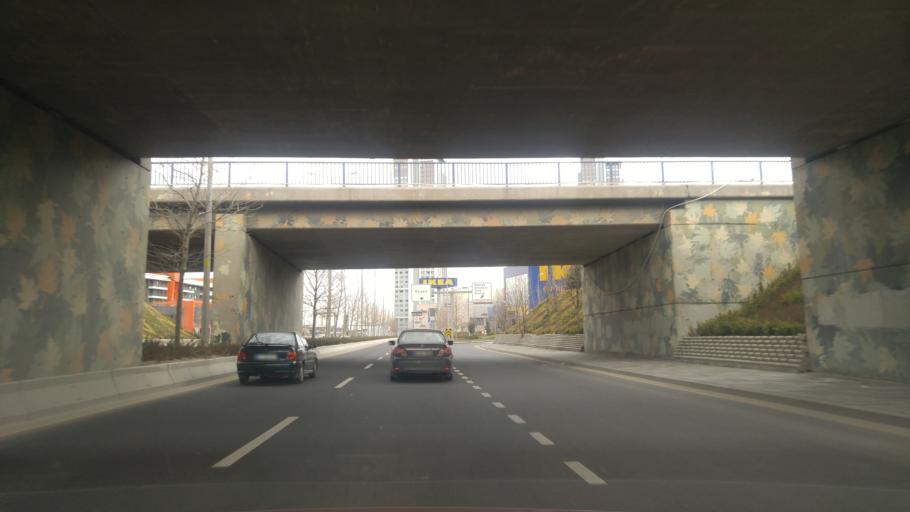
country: TR
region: Ankara
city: Mamak
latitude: 39.8880
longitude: 32.9295
